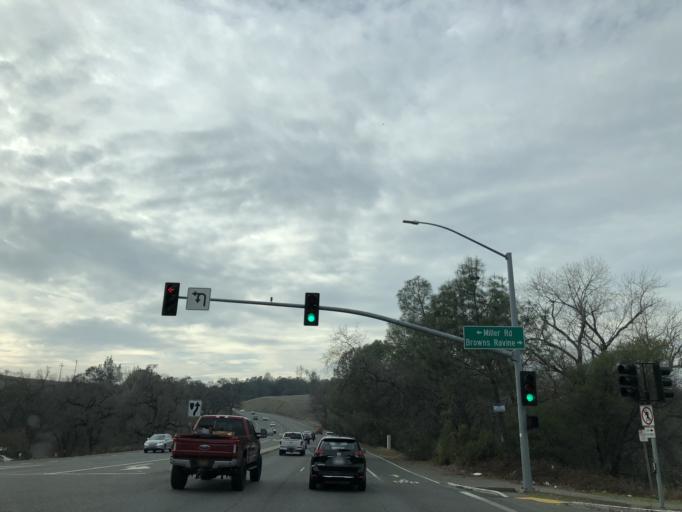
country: US
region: California
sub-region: El Dorado County
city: El Dorado Hills
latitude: 38.7089
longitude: -121.0918
